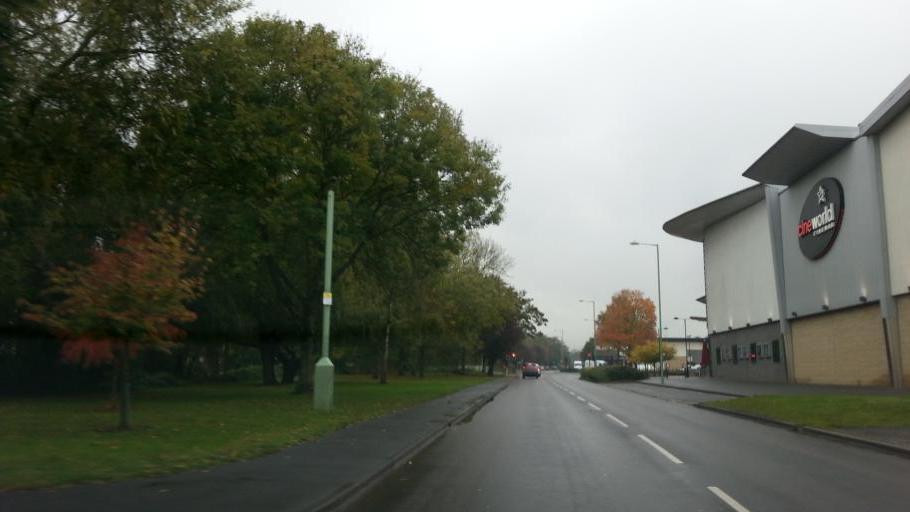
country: GB
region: England
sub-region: Suffolk
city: Haverhill
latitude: 52.0812
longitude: 0.4437
